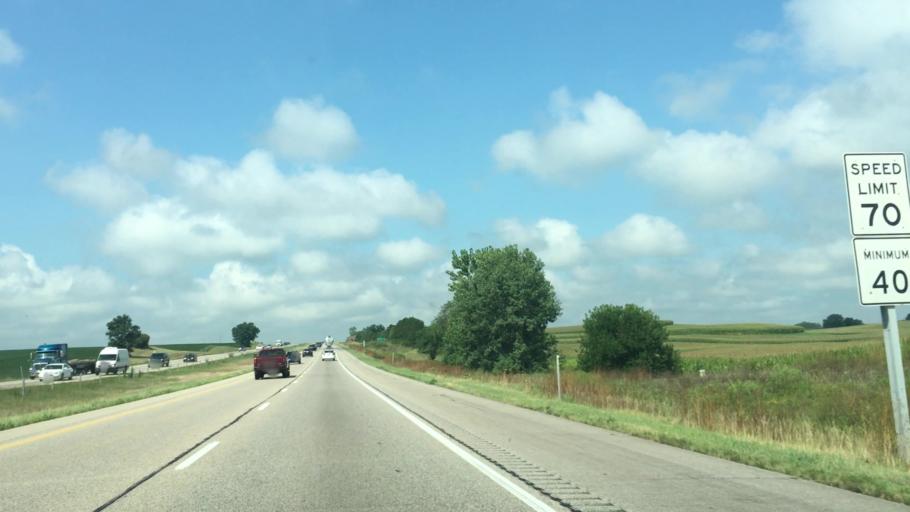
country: US
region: Iowa
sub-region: Cedar County
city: West Branch
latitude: 41.6639
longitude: -91.2609
